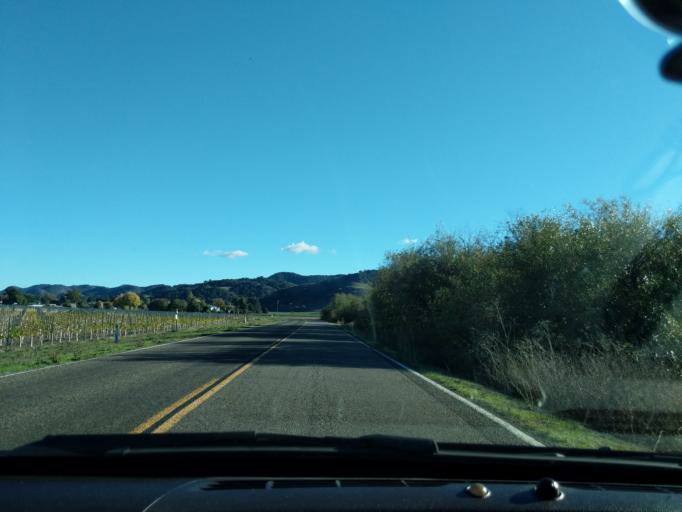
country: US
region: California
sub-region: Santa Barbara County
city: Los Alamos
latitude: 34.7482
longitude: -120.2900
